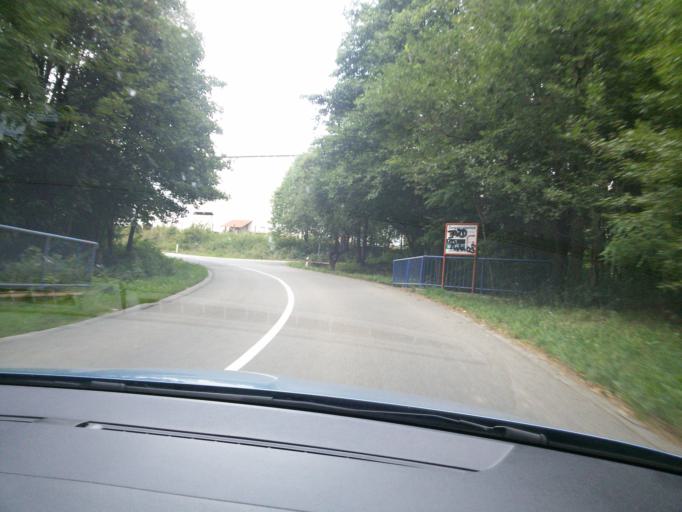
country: CZ
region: South Moravian
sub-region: Okres Brno-Venkov
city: Lomnice
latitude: 49.4115
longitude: 16.4107
